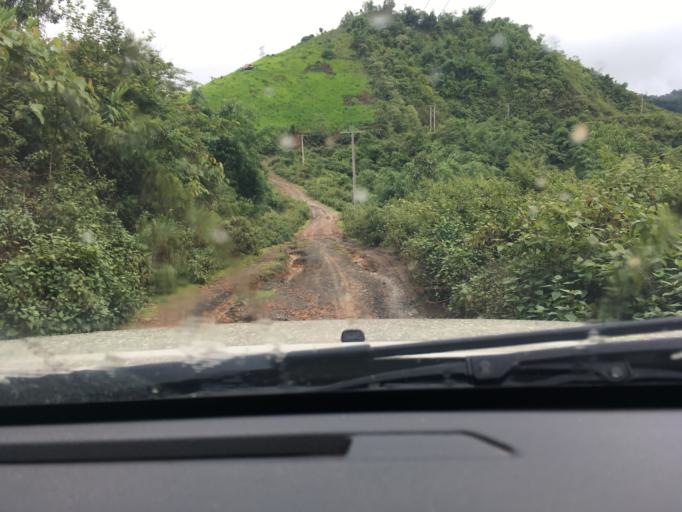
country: LA
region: Phongsali
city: Phongsali
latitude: 21.3575
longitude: 102.1174
